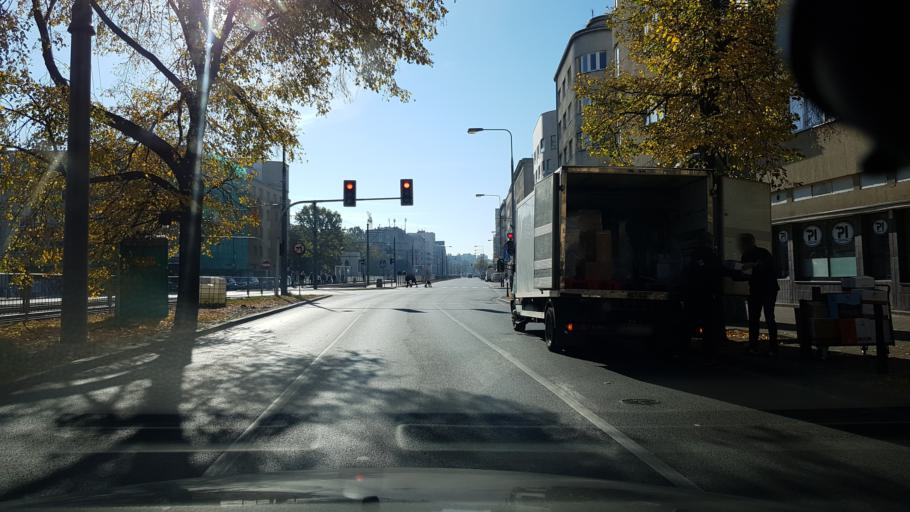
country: PL
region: Masovian Voivodeship
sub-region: Warszawa
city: Mokotow
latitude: 52.2060
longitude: 21.0225
